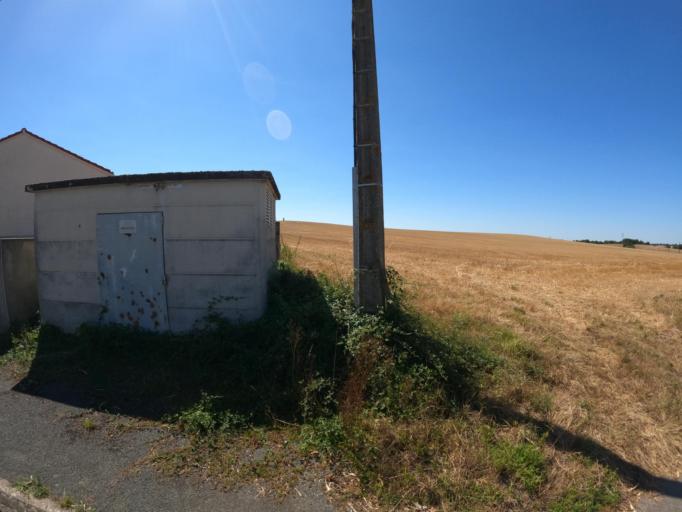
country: FR
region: Pays de la Loire
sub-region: Departement de Maine-et-Loire
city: Saint-Christophe-du-Bois
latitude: 47.0339
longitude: -0.9481
